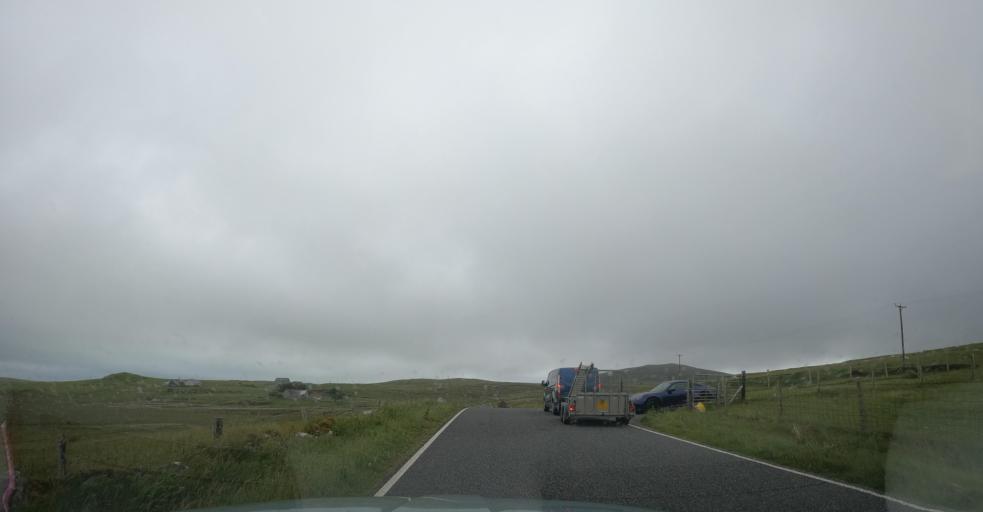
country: GB
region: Scotland
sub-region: Eilean Siar
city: Isle of North Uist
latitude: 57.6600
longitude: -7.2359
